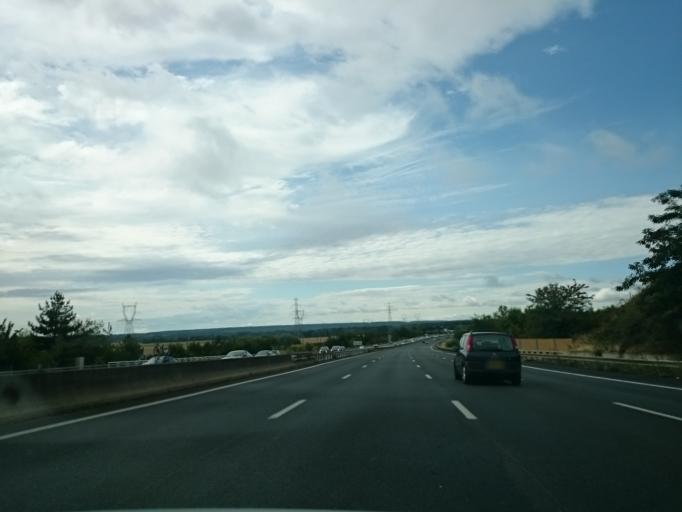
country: FR
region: Ile-de-France
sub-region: Departement de l'Essonne
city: Briis-sous-Forges
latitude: 48.6229
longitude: 2.1350
